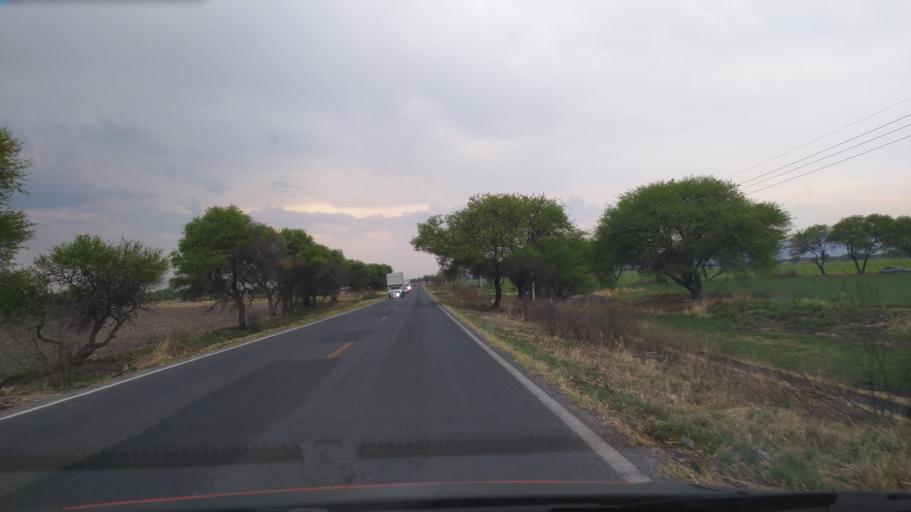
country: MX
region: Guanajuato
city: Ciudad Manuel Doblado
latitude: 20.7551
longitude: -101.9208
